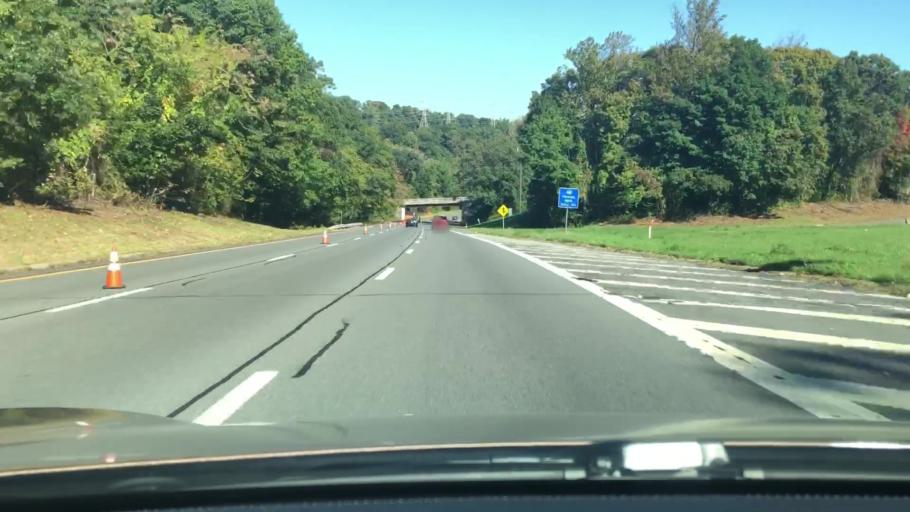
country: US
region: New York
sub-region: Westchester County
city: Greenville
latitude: 40.9860
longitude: -73.8386
